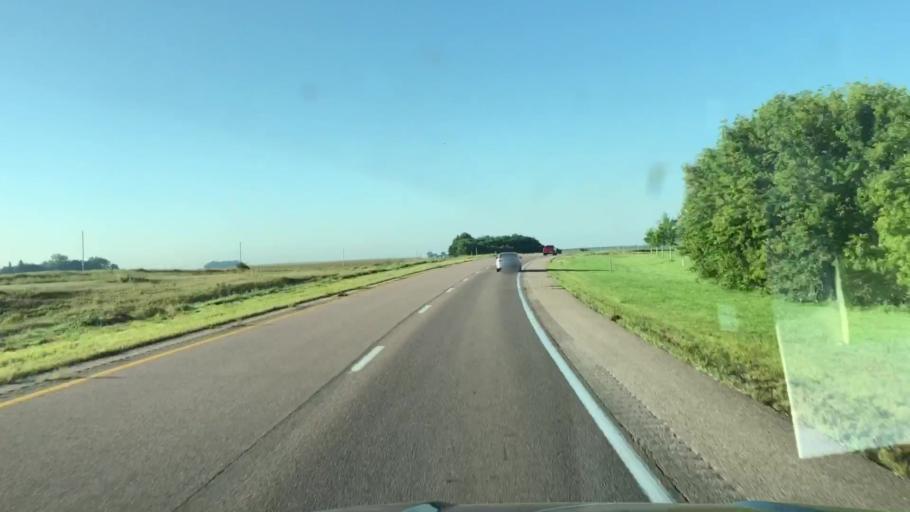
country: US
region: Iowa
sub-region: O'Brien County
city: Sheldon
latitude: 43.1342
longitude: -95.8810
